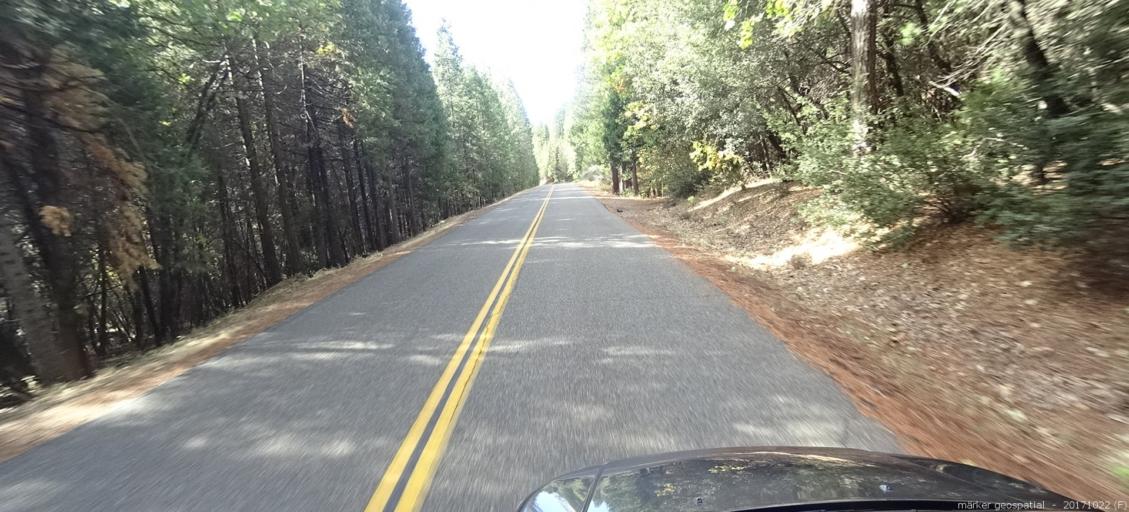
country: US
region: California
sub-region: Siskiyou County
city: Dunsmuir
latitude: 41.0704
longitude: -122.3572
